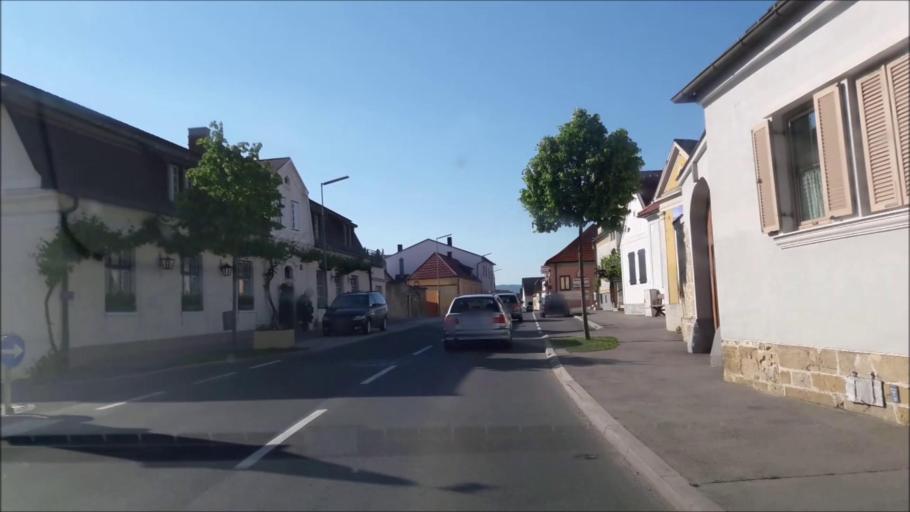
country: AT
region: Burgenland
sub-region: Eisenstadt-Umgebung
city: Sankt Margarethen im Burgenland
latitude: 47.8052
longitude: 16.6076
